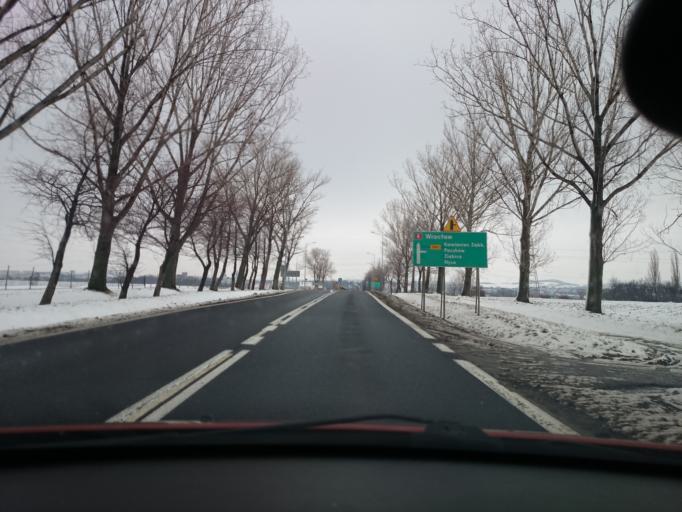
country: PL
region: Lower Silesian Voivodeship
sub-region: Powiat zabkowicki
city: Zabkowice Slaskie
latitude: 50.5782
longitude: 16.8004
